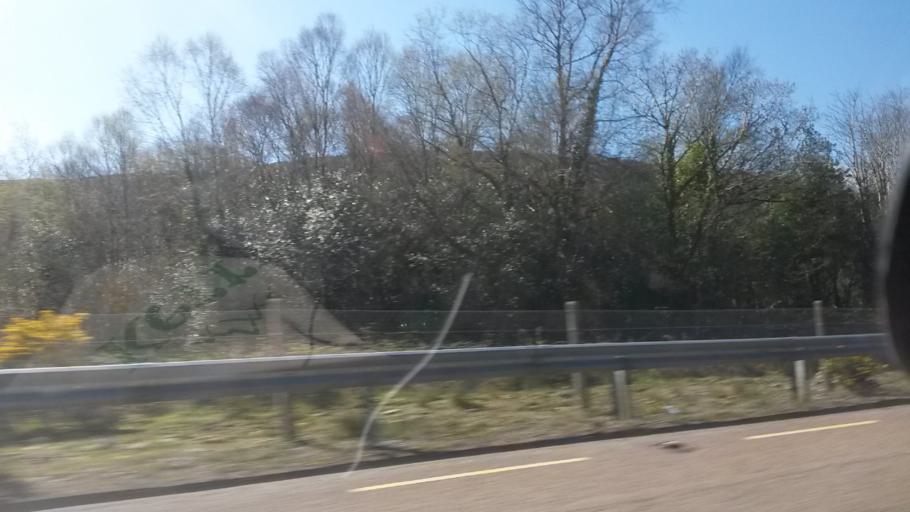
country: IE
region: Munster
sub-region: Ciarrai
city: Cill Airne
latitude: 51.9636
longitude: -9.3604
